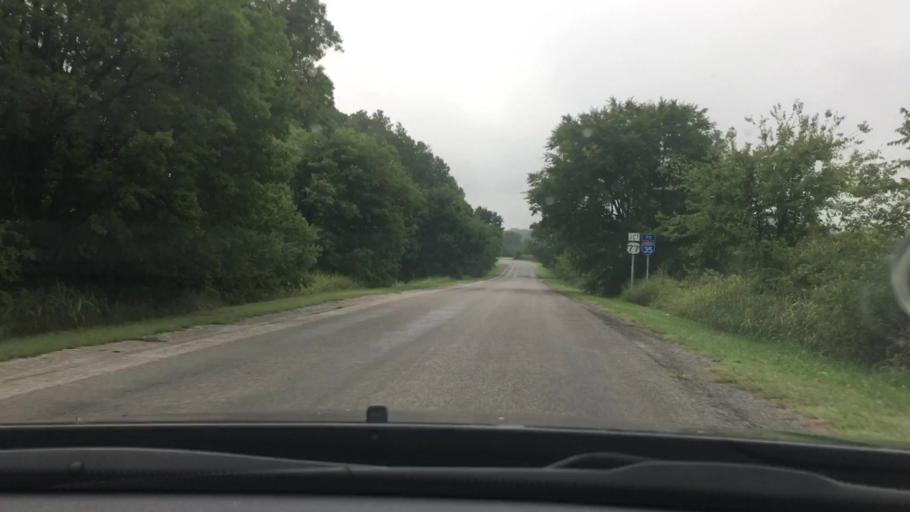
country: US
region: Oklahoma
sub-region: Murray County
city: Davis
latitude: 34.4548
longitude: -97.1372
